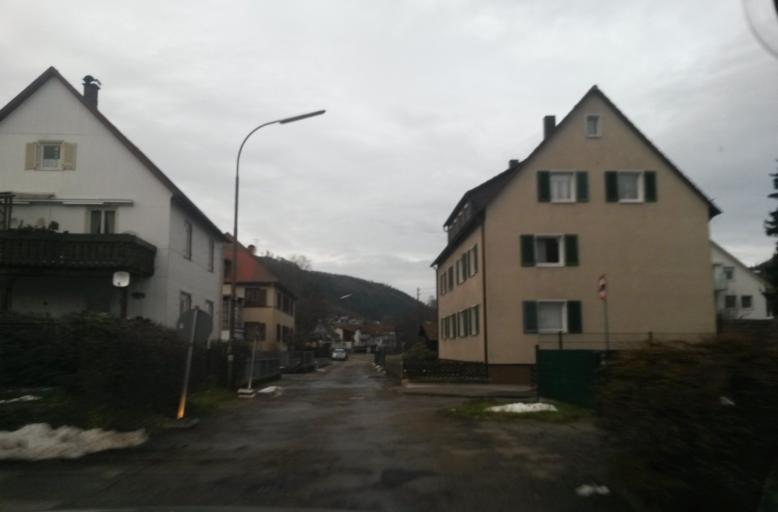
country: DE
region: Baden-Wuerttemberg
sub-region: Karlsruhe Region
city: Hofen an der Enz
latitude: 48.7785
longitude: 8.5748
